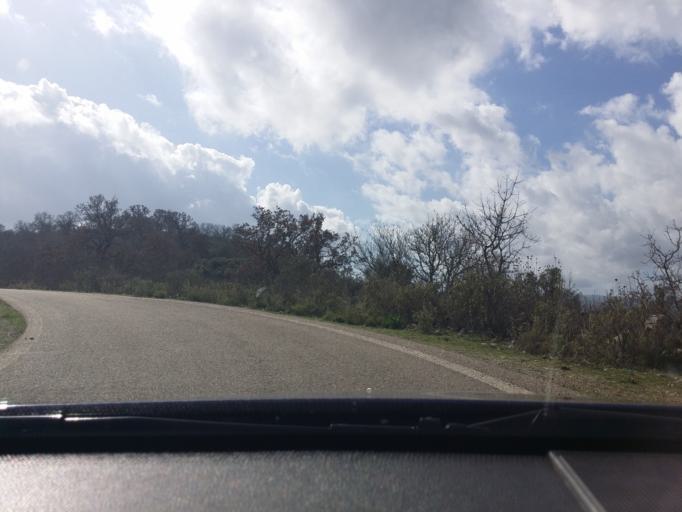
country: GR
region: West Greece
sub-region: Nomos Aitolias kai Akarnanias
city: Fitiai
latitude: 38.6418
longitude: 21.1959
